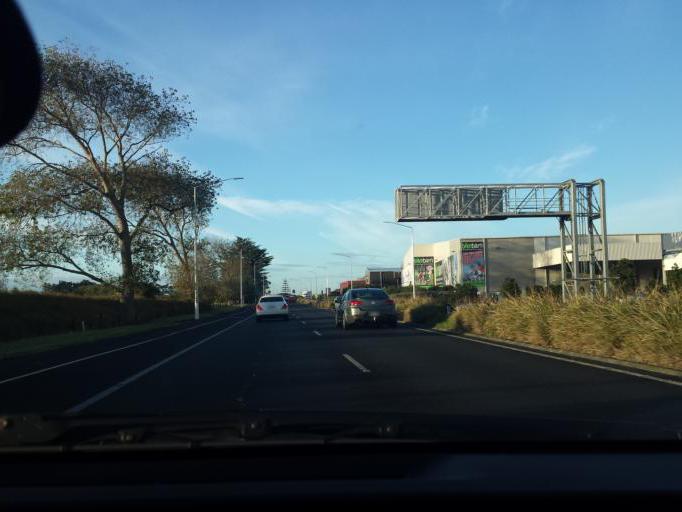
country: NZ
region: Auckland
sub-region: Auckland
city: Mangere
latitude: -36.9870
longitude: 174.7857
